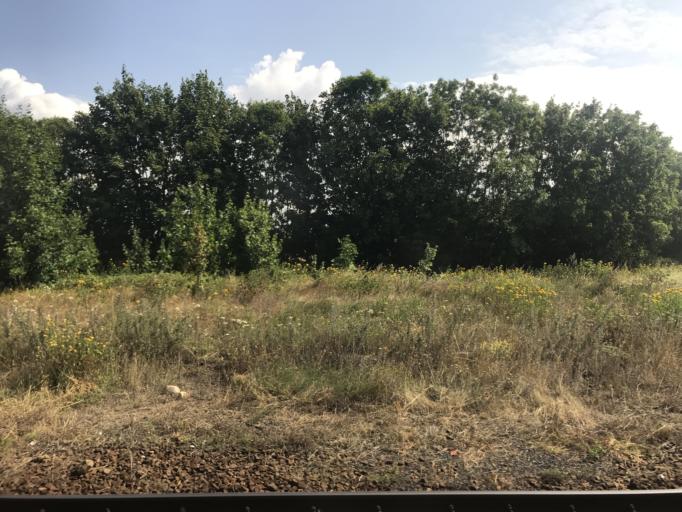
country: PL
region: Kujawsko-Pomorskie
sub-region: Powiat inowroclawski
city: Zlotniki Kujawskie
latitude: 52.9060
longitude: 18.1448
